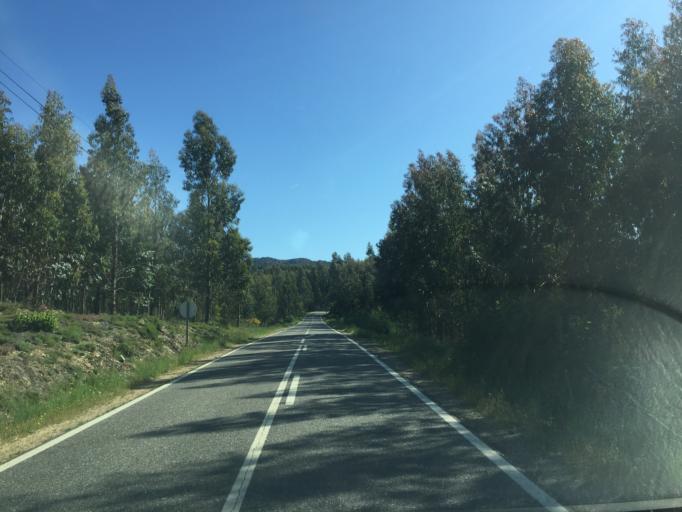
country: PT
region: Coimbra
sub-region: Pampilhosa da Serra
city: Pampilhosa da Serra
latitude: 40.0530
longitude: -7.8667
